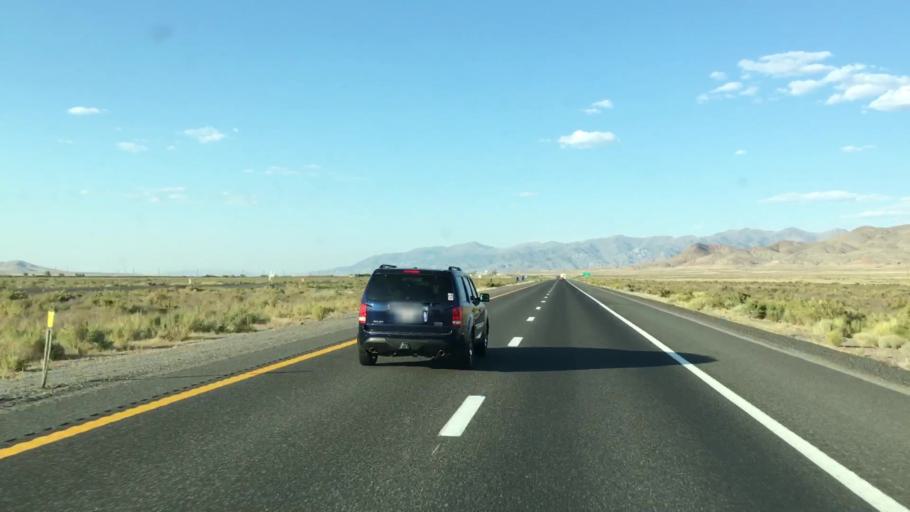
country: US
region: Nevada
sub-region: Pershing County
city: Lovelock
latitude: 40.2286
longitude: -118.3994
